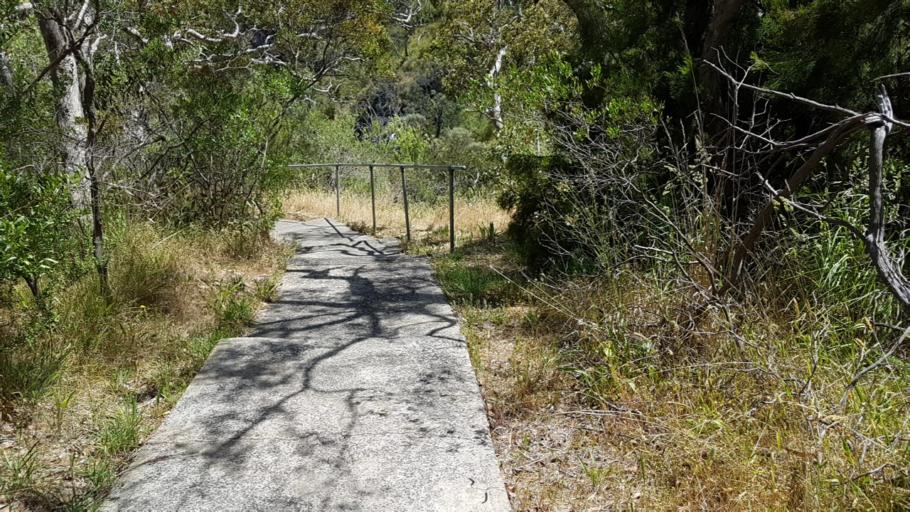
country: AU
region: South Australia
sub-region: Alexandrina
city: Mount Compass
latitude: -35.4428
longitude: 138.5842
